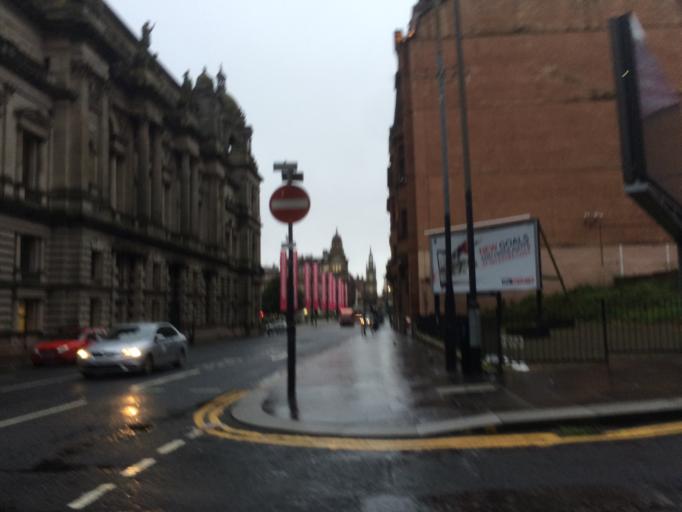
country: GB
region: Scotland
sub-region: Glasgow City
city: Glasgow
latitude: 55.8613
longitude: -4.2472
